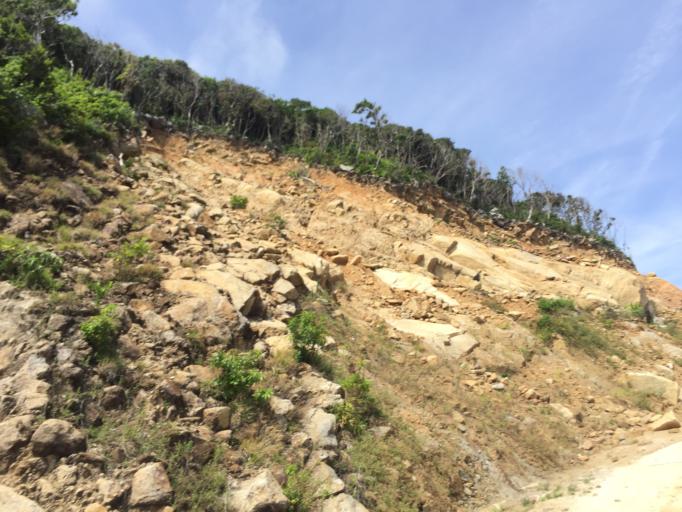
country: VN
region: Quang Nam
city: Hoi An
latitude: 15.9750
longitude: 108.5054
